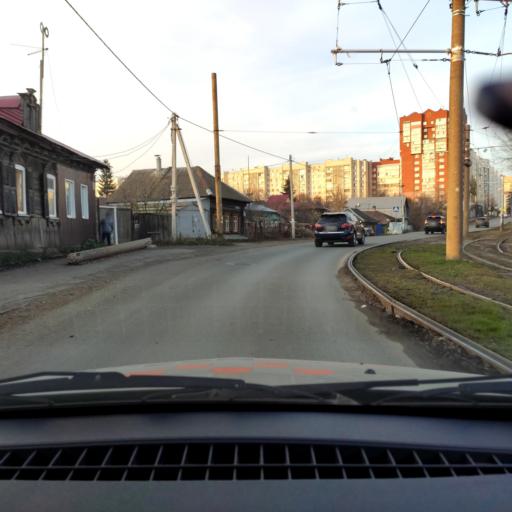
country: RU
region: Bashkortostan
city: Ufa
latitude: 54.7240
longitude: 55.9659
